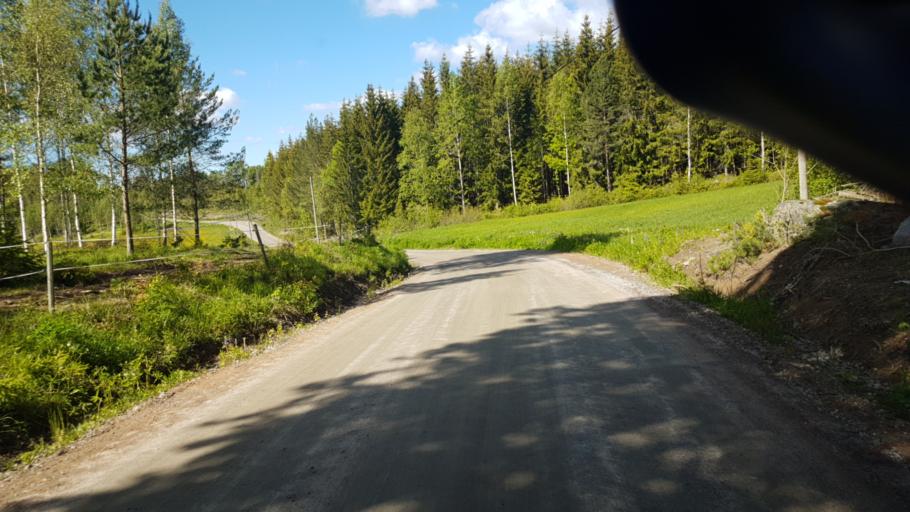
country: SE
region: Vaermland
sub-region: Arvika Kommun
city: Arvika
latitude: 59.5318
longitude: 12.8458
